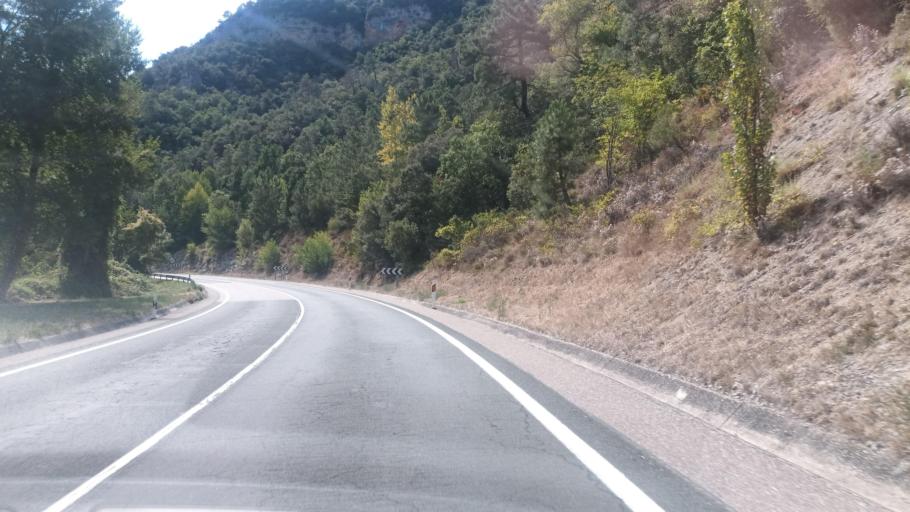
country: ES
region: Castille and Leon
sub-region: Provincia de Burgos
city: Trespaderne
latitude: 42.7845
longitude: -3.4260
